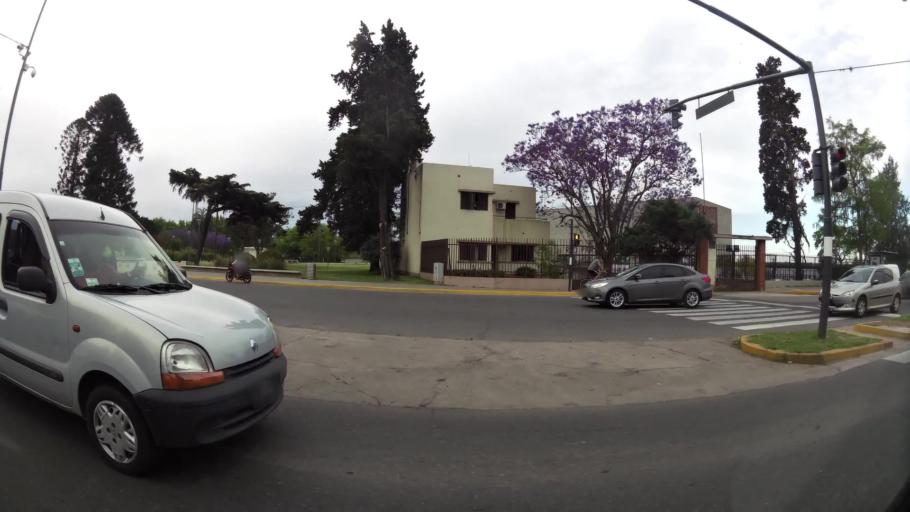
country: AR
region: Santa Fe
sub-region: Departamento de Rosario
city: Rosario
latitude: -32.9122
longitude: -60.6754
